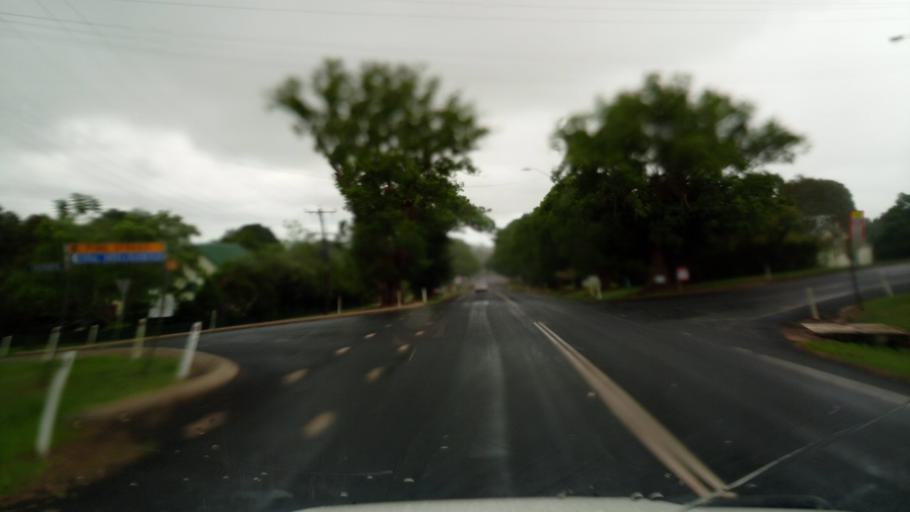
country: AU
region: Queensland
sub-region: Tablelands
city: Tolga
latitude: -17.2737
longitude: 145.5854
